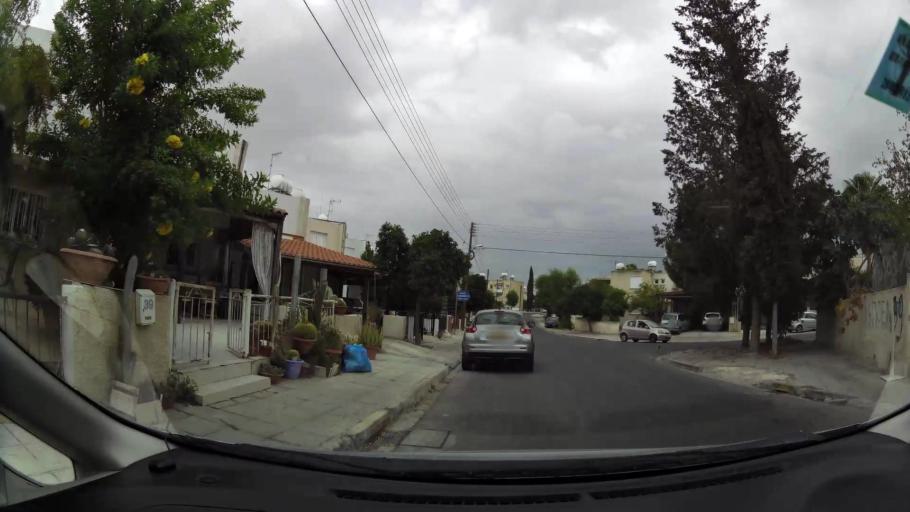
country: CY
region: Lefkosia
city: Geri
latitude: 35.1132
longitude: 33.3867
